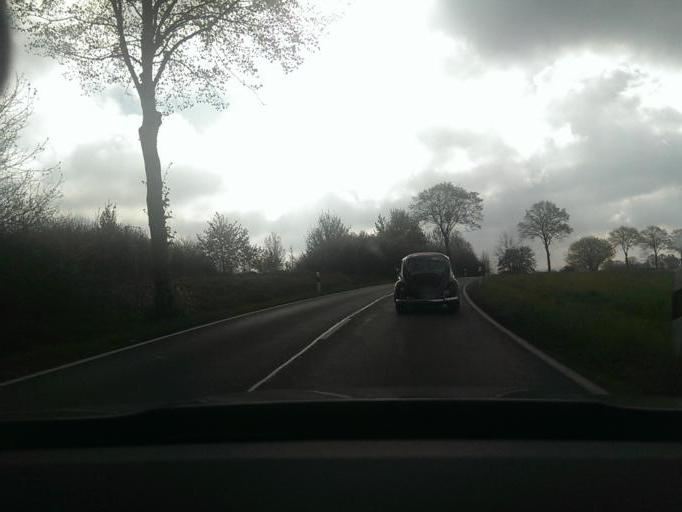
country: DE
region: Lower Saxony
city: Hameln
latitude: 52.1558
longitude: 9.3740
